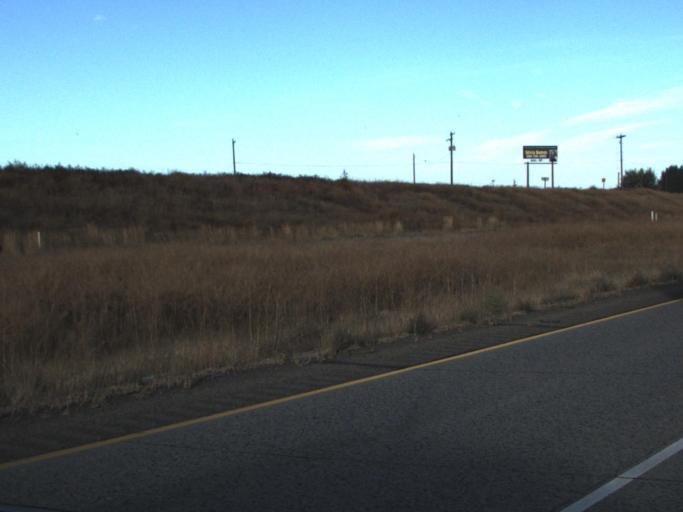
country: US
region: Washington
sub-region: Yakima County
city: Grandview
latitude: 46.2784
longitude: -119.9346
